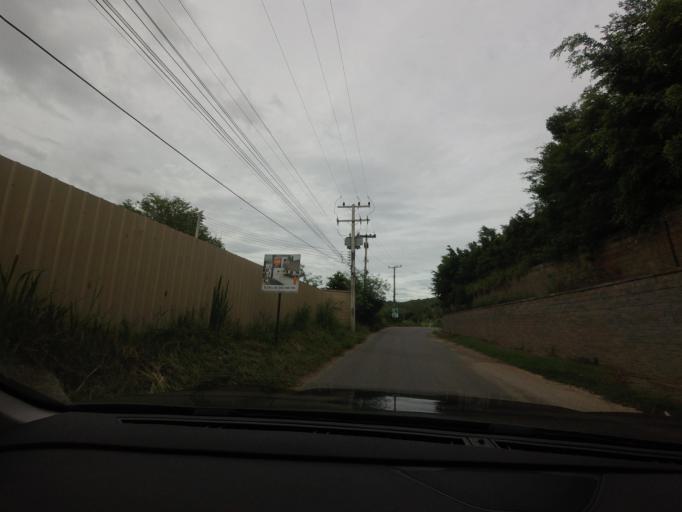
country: TH
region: Prachuap Khiri Khan
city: Hua Hin
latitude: 12.5252
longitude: 99.9398
